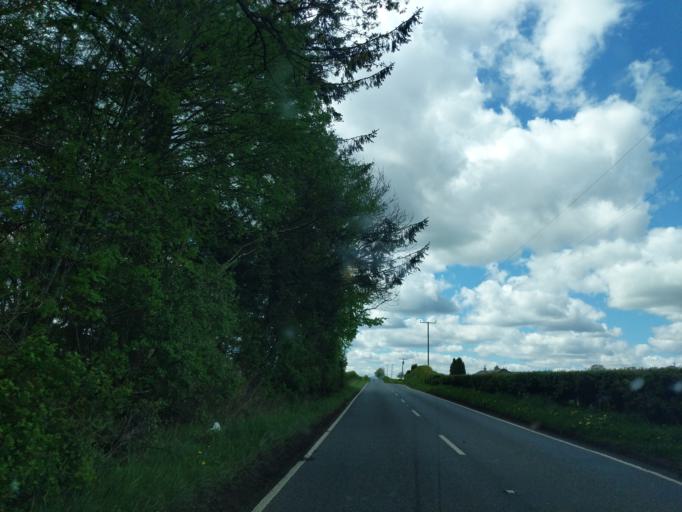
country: GB
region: Scotland
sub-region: Stirling
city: Doune
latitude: 56.1673
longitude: -4.1021
